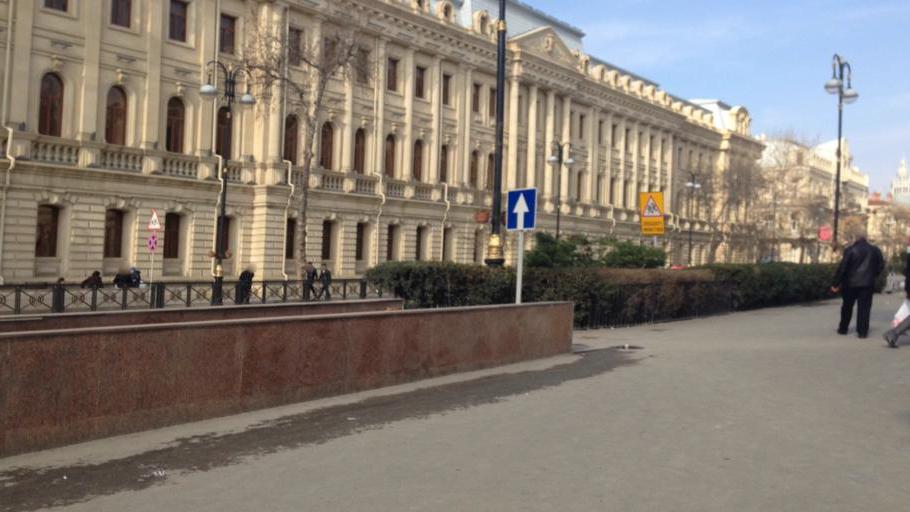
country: AZ
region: Baki
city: Badamdar
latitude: 40.3660
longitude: 49.8312
